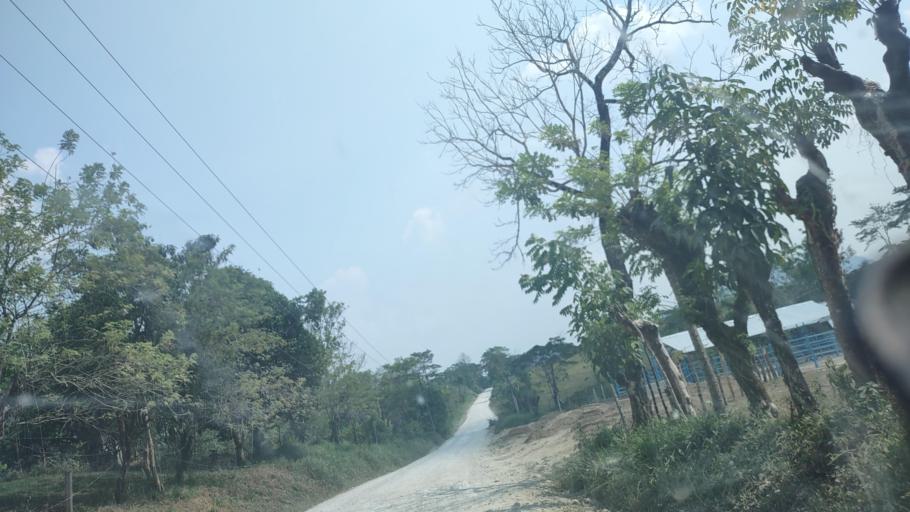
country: MX
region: Tabasco
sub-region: Huimanguillo
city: Francisco Rueda
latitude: 17.5884
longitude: -93.8919
